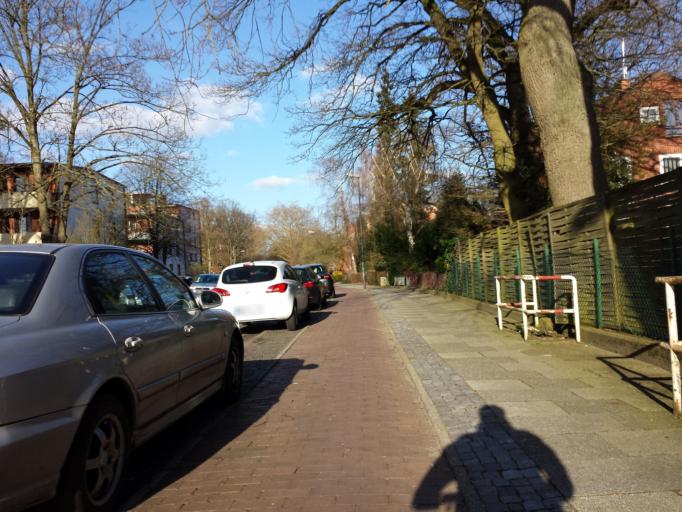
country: DE
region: Bremen
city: Bremen
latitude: 53.0878
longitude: 8.8503
